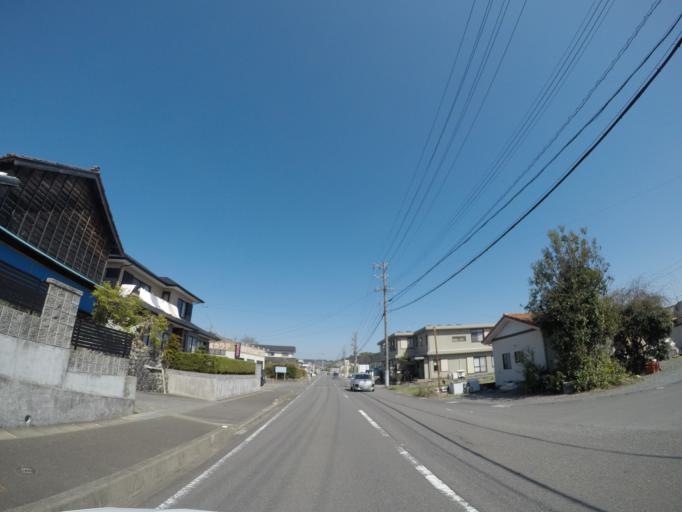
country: JP
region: Shizuoka
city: Kanaya
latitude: 34.7688
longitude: 138.1056
